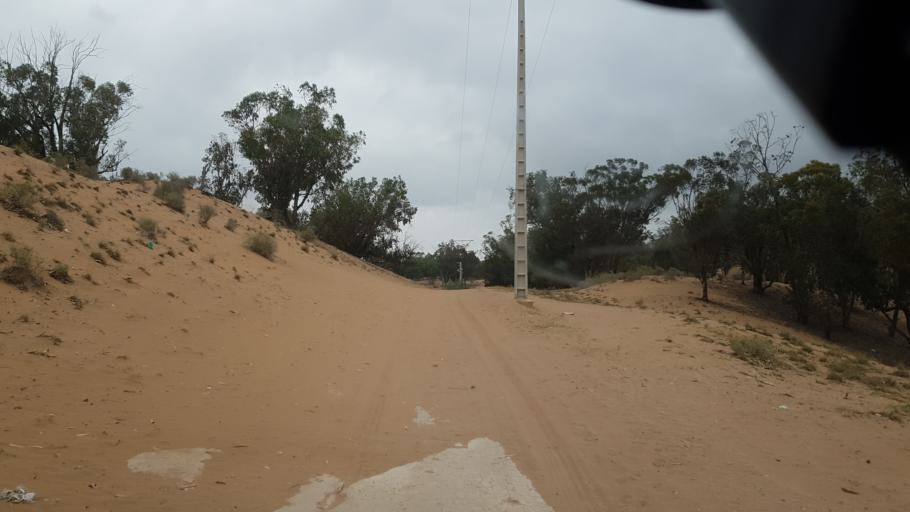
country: MA
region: Souss-Massa-Draa
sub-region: Inezgane-Ait Mellou
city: Inezgane
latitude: 30.3170
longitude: -9.5378
